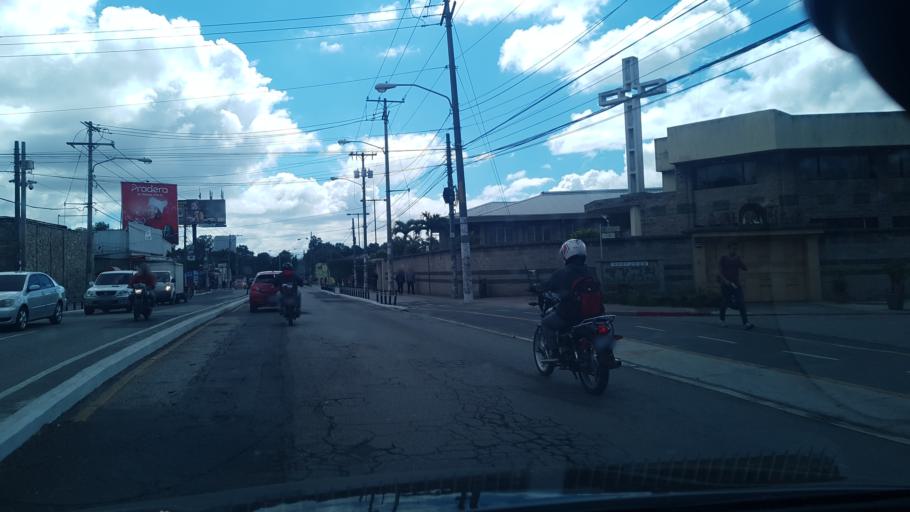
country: GT
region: Guatemala
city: Santa Catarina Pinula
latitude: 14.5927
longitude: -90.5510
